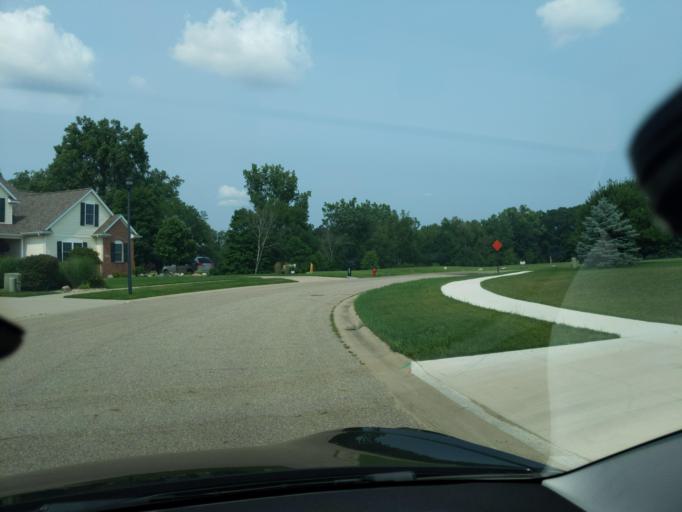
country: US
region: Michigan
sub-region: Ingham County
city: Holt
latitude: 42.6308
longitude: -84.5559
